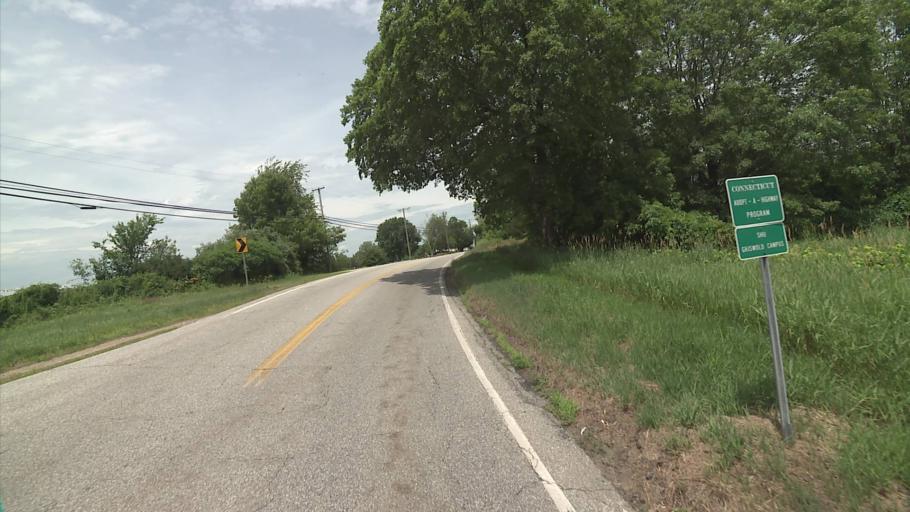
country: US
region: Connecticut
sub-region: New London County
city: Jewett City
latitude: 41.5765
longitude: -71.9770
